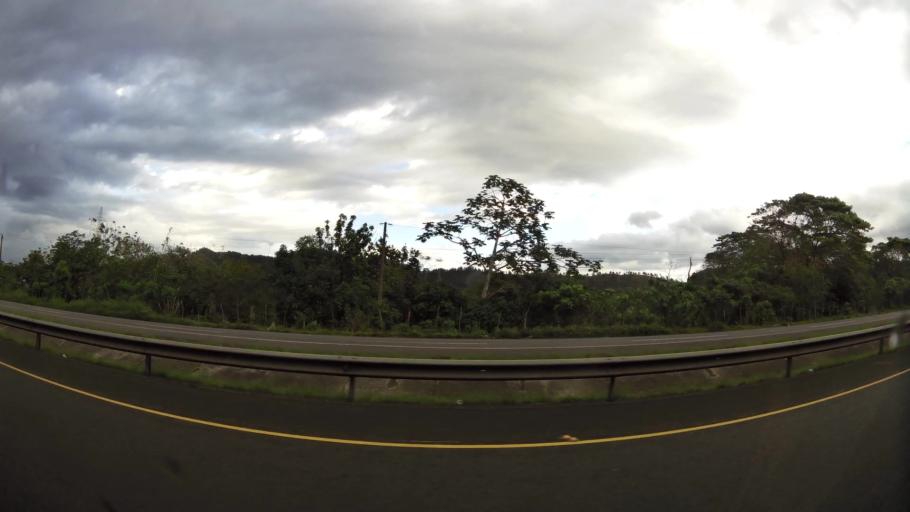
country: DO
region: Monsenor Nouel
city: Bonao
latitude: 18.9293
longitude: -70.3844
